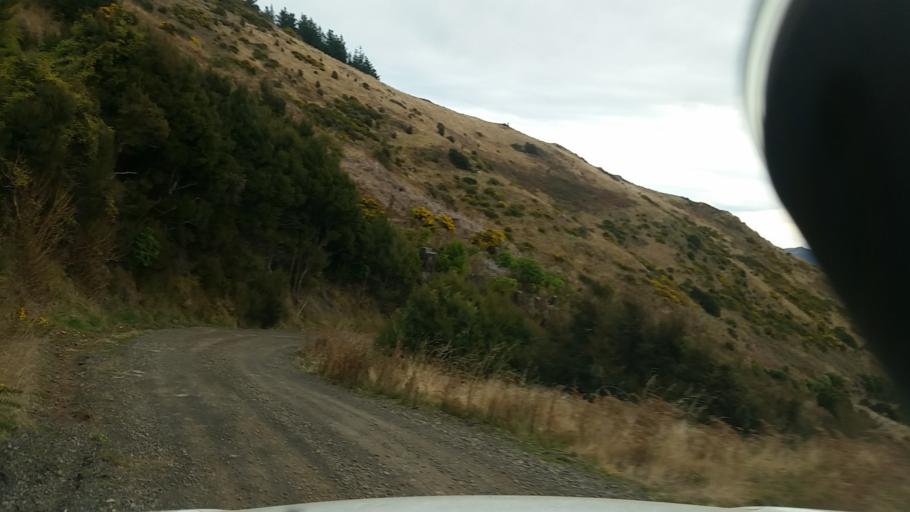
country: NZ
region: Canterbury
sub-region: Christchurch City
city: Christchurch
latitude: -43.8295
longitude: 172.9921
